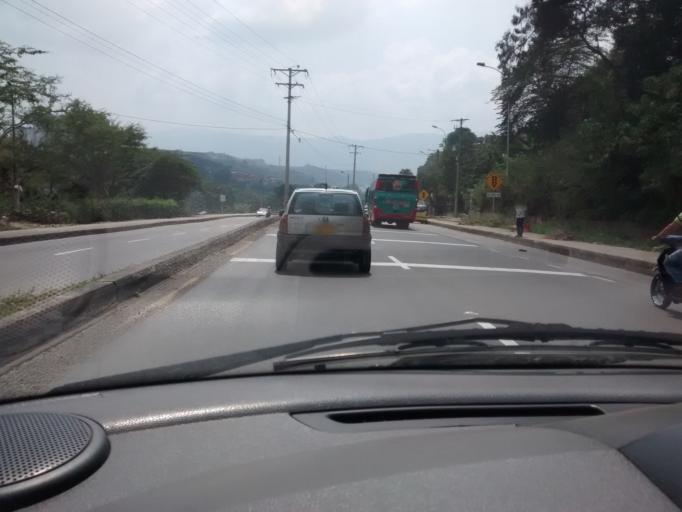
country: CO
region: Santander
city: Bucaramanga
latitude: 7.0946
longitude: -73.1188
